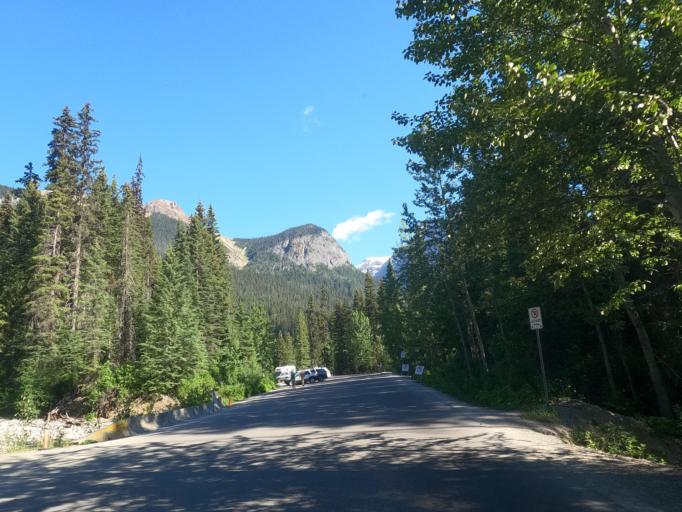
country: CA
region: Alberta
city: Lake Louise
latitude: 51.4375
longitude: -116.5403
